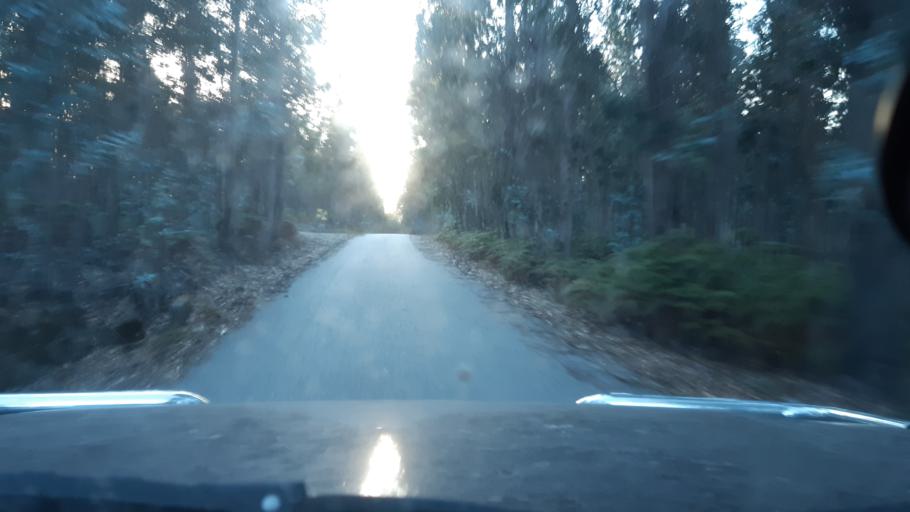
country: PT
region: Aveiro
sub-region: Agueda
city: Aguada de Cima
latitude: 40.5533
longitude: -8.2859
